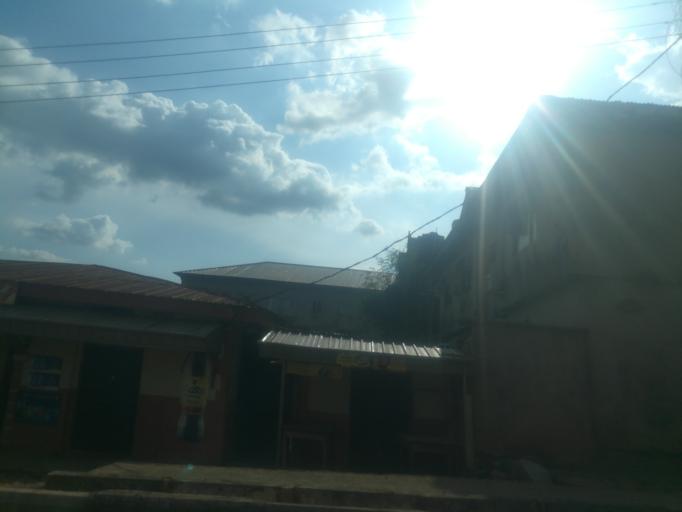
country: NG
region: Oyo
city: Ibadan
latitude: 7.4215
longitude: 3.8443
